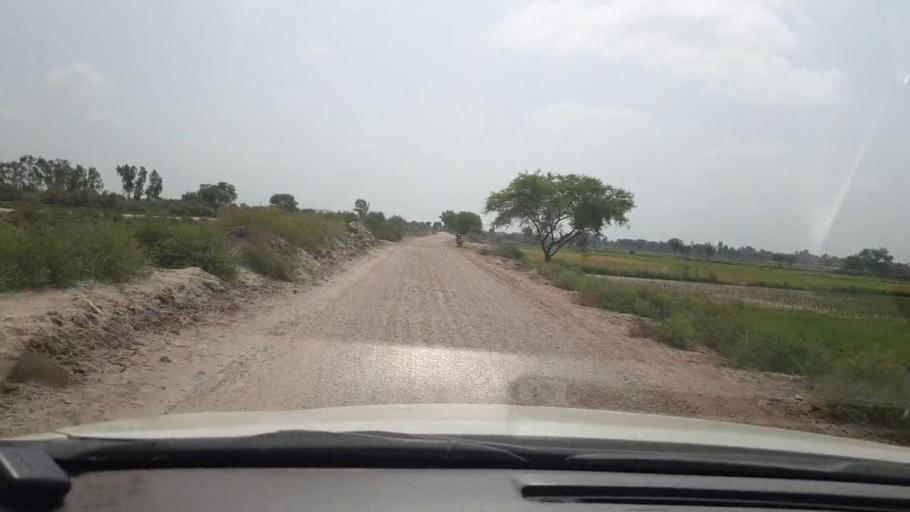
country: PK
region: Sindh
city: Shikarpur
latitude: 28.0098
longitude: 68.5666
